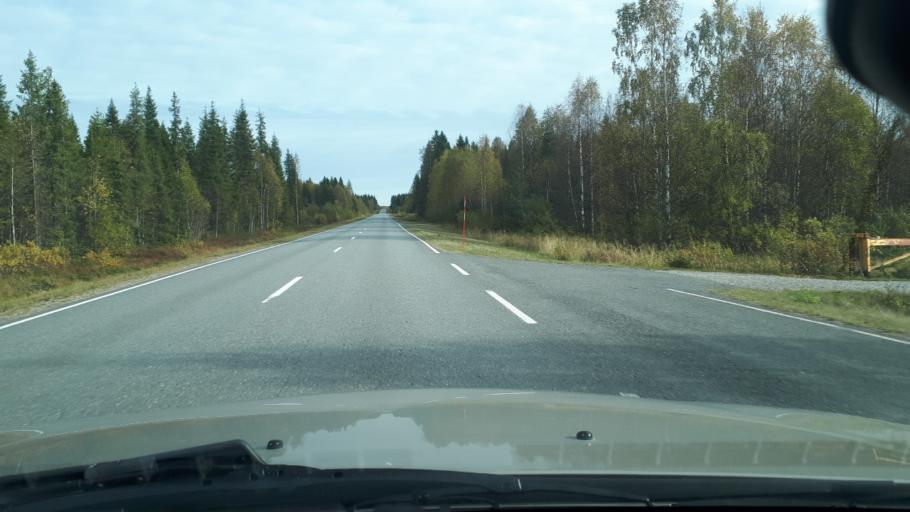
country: FI
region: Lapland
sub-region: Rovaniemi
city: Ranua
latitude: 65.9695
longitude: 26.0963
